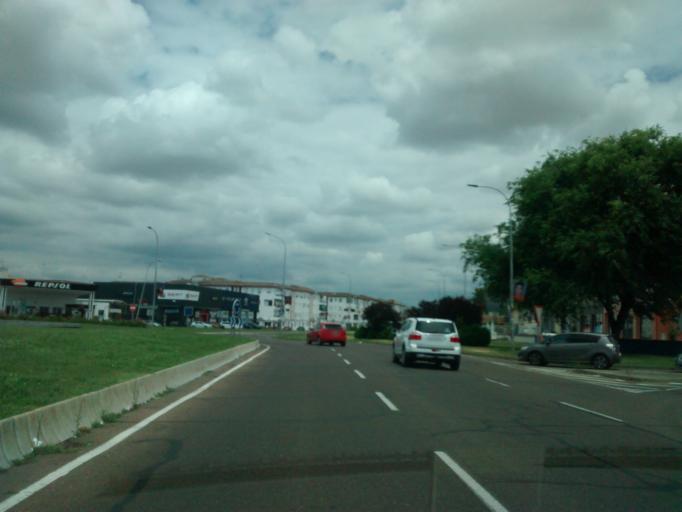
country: ES
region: Extremadura
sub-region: Provincia de Badajoz
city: Merida
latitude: 38.9240
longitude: -6.3268
